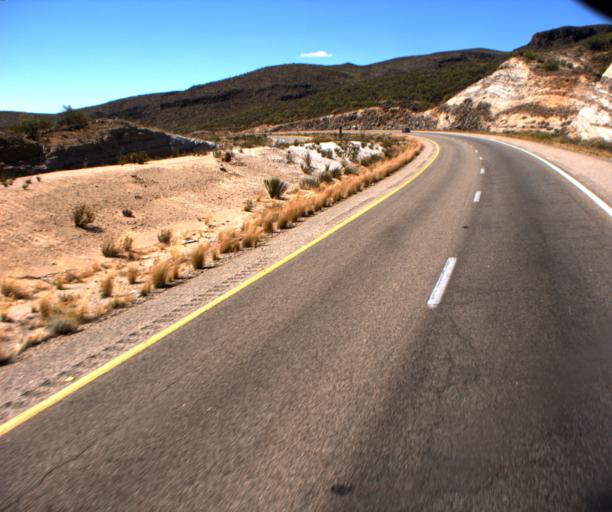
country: US
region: Arizona
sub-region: Yavapai County
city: Bagdad
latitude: 34.5646
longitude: -113.4576
